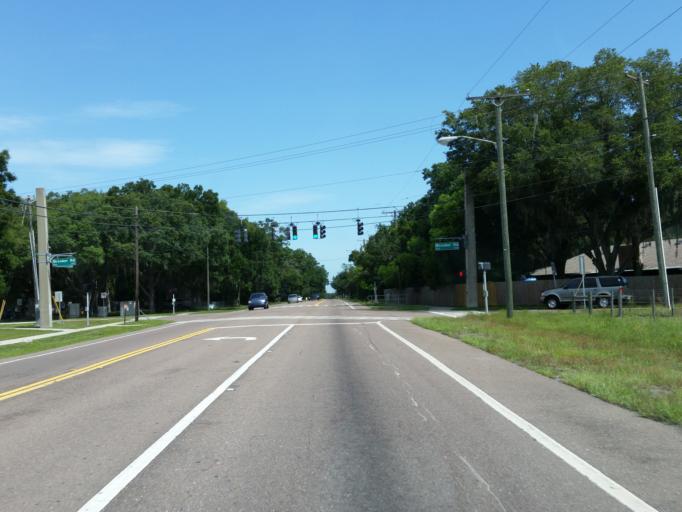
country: US
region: Florida
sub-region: Hillsborough County
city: Bloomingdale
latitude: 27.9079
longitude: -82.2564
